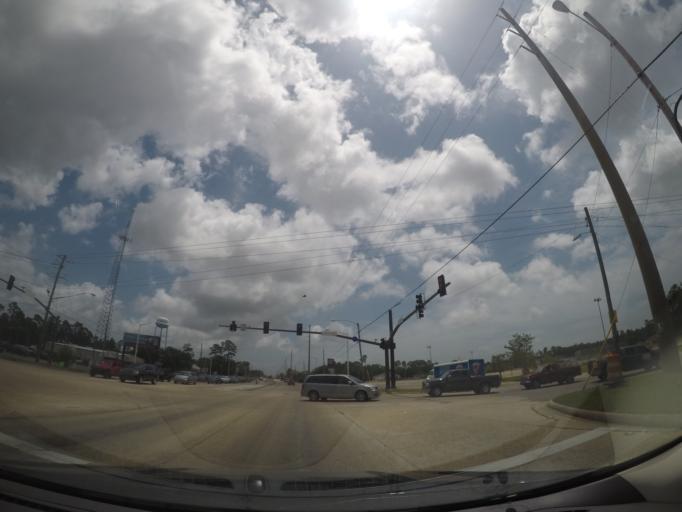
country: US
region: Mississippi
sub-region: Hancock County
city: Waveland
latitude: 30.2994
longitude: -89.3977
